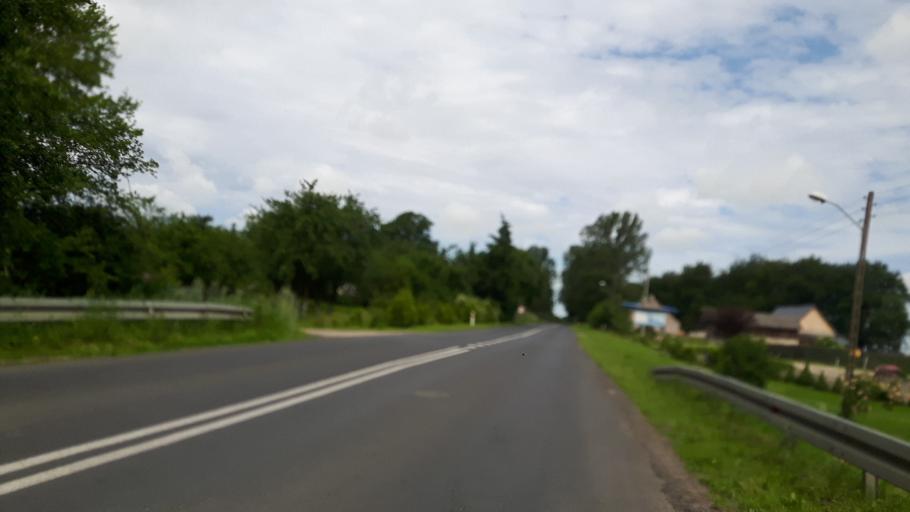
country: PL
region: West Pomeranian Voivodeship
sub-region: Powiat gryficki
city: Trzebiatow
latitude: 54.0145
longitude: 15.2437
